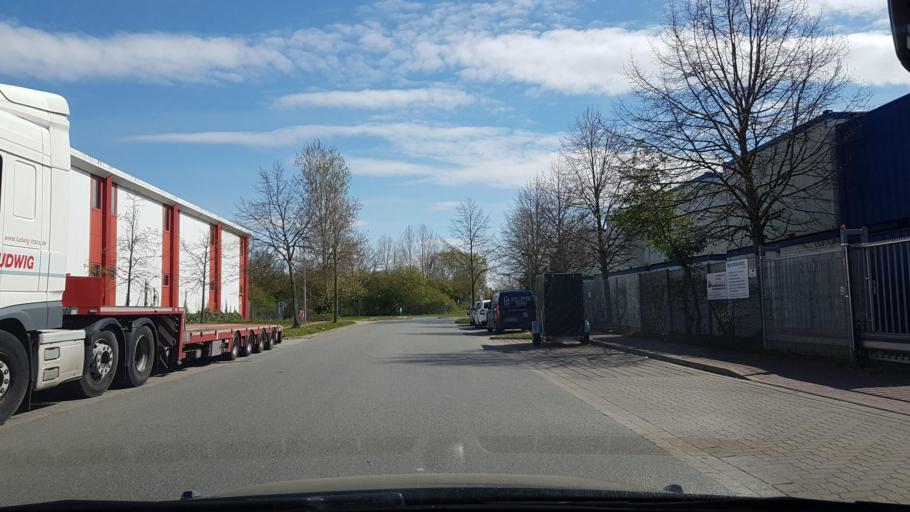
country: DE
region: Lower Saxony
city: Garbsen-Mitte
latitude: 52.4477
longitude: 9.5924
